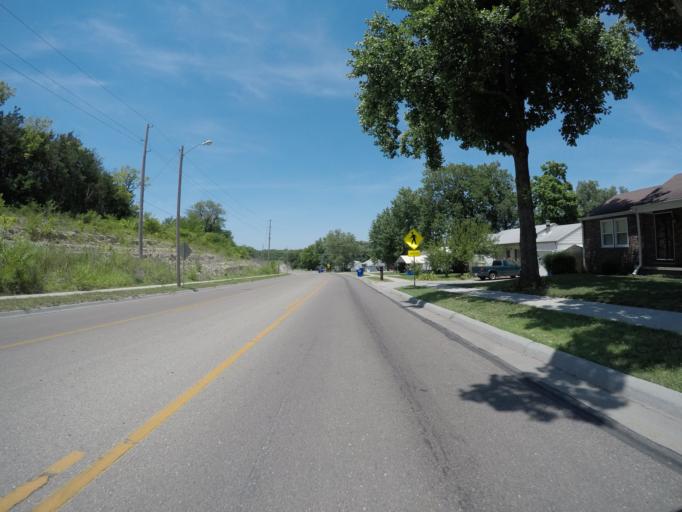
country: US
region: Kansas
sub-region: Geary County
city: Junction City
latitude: 39.0307
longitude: -96.8547
